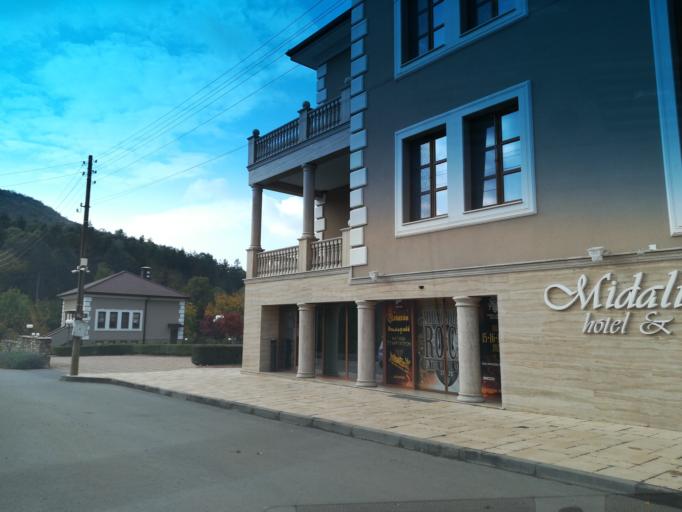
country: BG
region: Stara Zagora
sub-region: Obshtina Nikolaevo
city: Elkhovo
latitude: 42.3411
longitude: 25.3993
